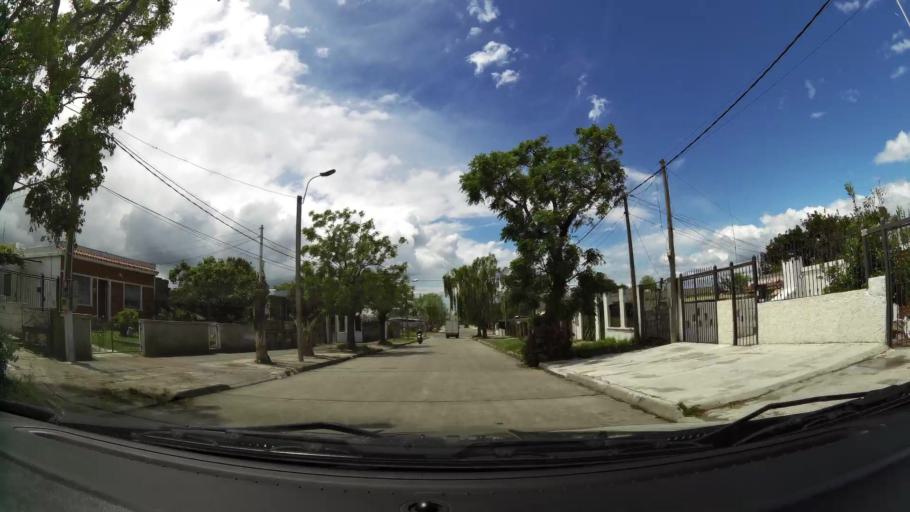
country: UY
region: Montevideo
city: Montevideo
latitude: -34.8793
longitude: -56.1256
